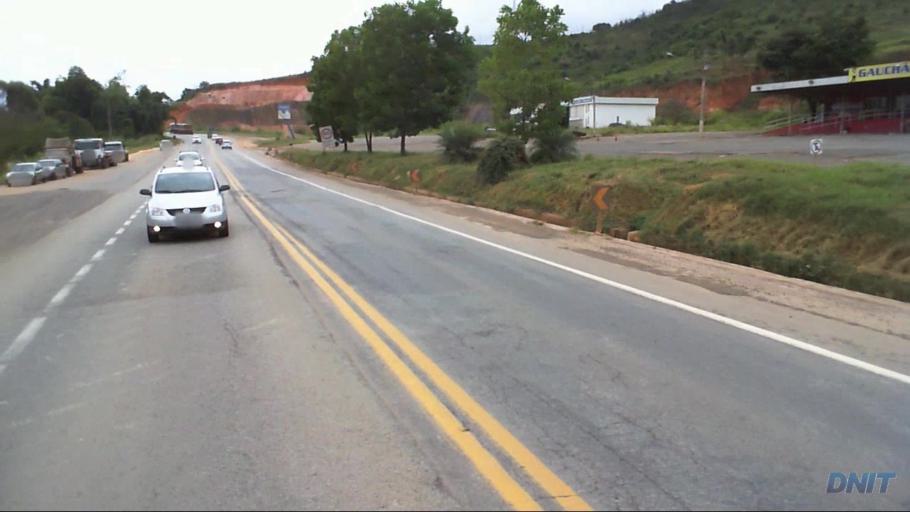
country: BR
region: Minas Gerais
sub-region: Joao Monlevade
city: Joao Monlevade
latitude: -19.8473
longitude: -43.2055
